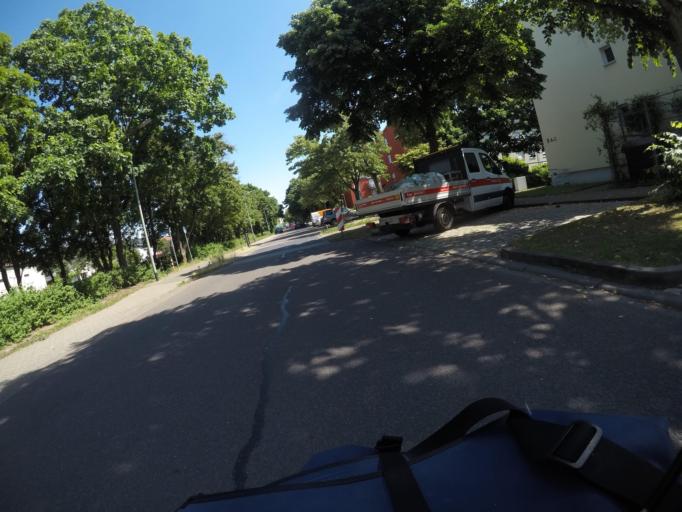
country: DE
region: Baden-Wuerttemberg
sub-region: Karlsruhe Region
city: Karlsruhe
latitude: 48.9958
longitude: 8.3530
